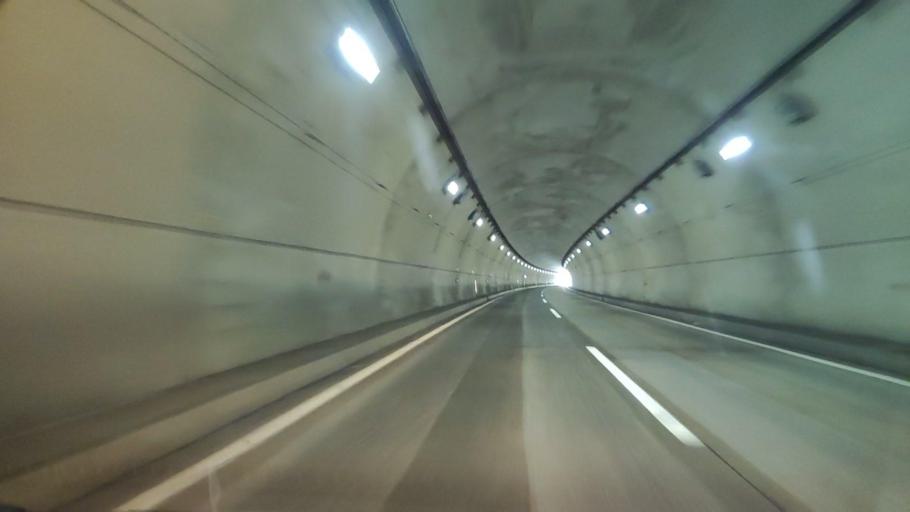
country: JP
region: Iwate
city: Ichinohe
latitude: 40.2252
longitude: 141.2651
